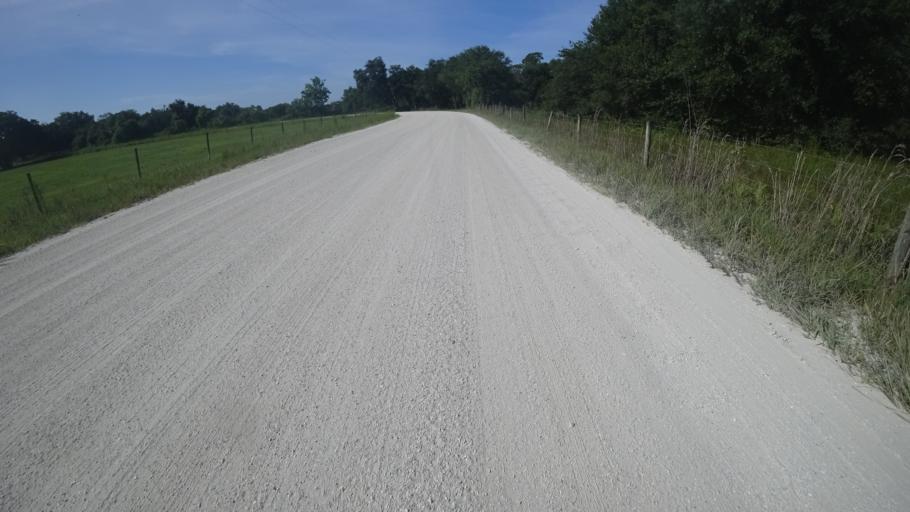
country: US
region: Florida
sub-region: Sarasota County
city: Lake Sarasota
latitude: 27.3366
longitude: -82.2053
